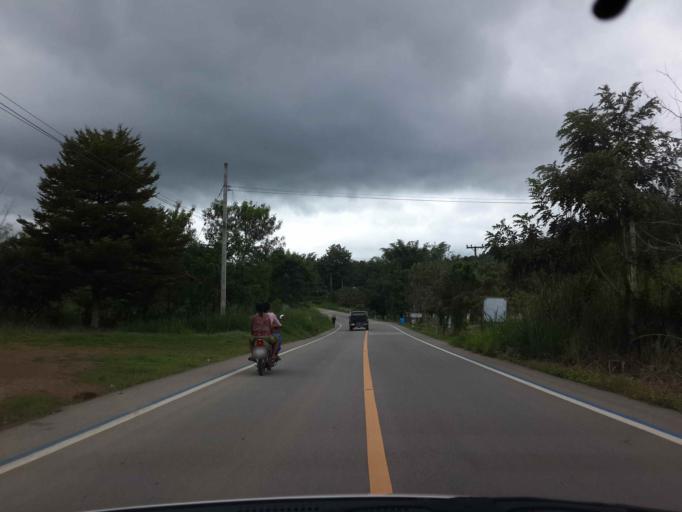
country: TH
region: Ratchaburi
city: Suan Phueng
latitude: 13.6496
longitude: 99.2119
